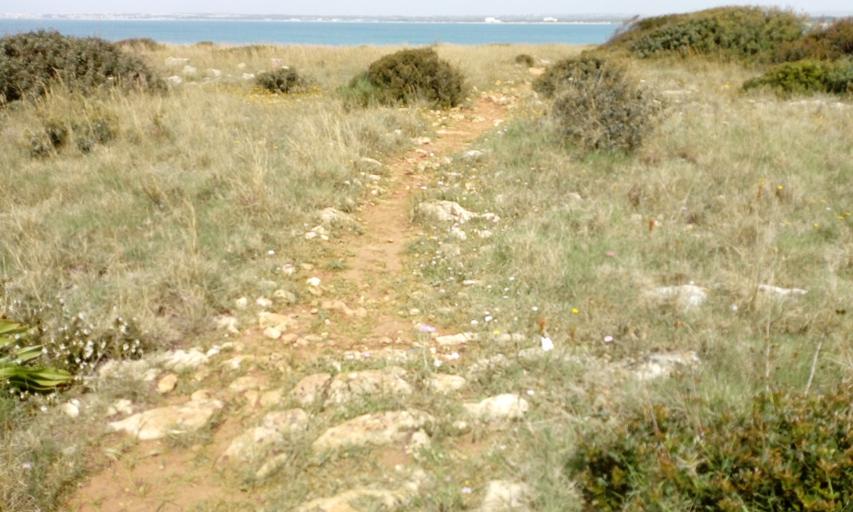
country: IT
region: Apulia
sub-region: Provincia di Lecce
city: Gallipoli
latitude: 39.9969
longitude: 17.9993
